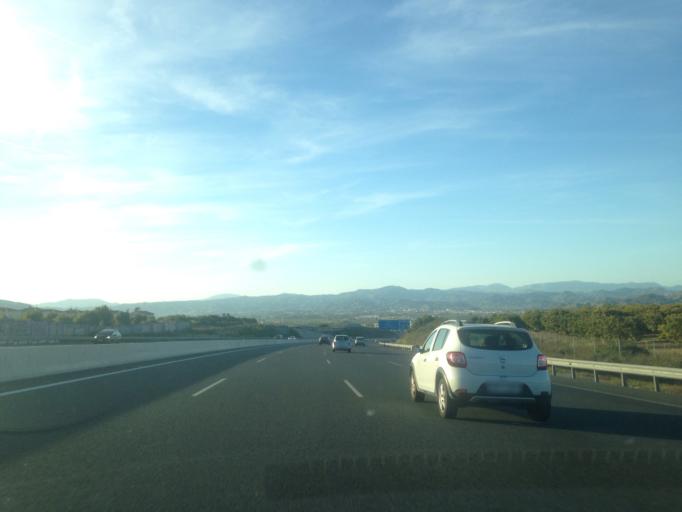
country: ES
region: Andalusia
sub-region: Provincia de Malaga
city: Alhaurin de la Torre
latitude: 36.6628
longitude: -4.5276
